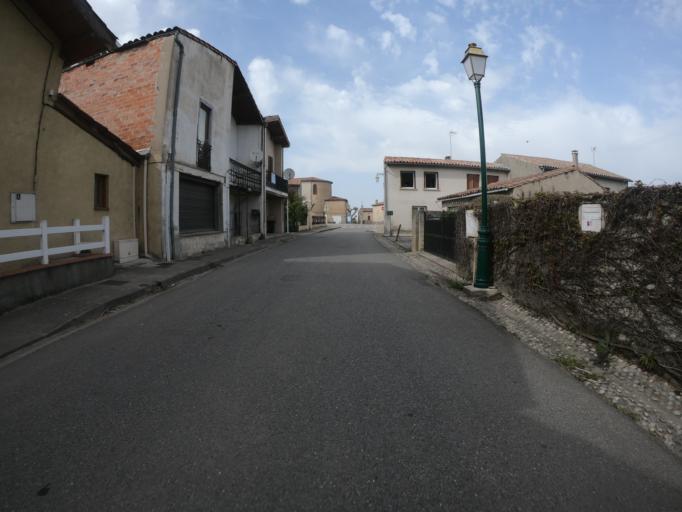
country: FR
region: Midi-Pyrenees
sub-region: Departement de l'Ariege
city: La Tour-du-Crieu
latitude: 43.1101
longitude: 1.7231
